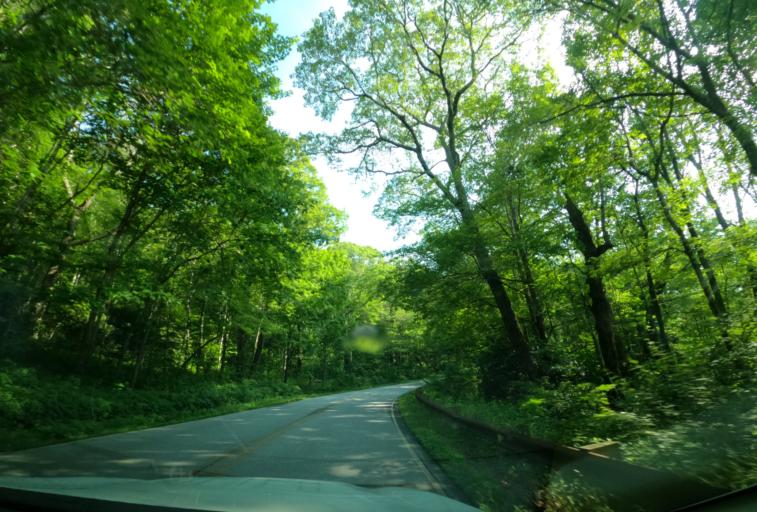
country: US
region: North Carolina
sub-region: Transylvania County
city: Brevard
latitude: 35.2723
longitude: -82.9192
